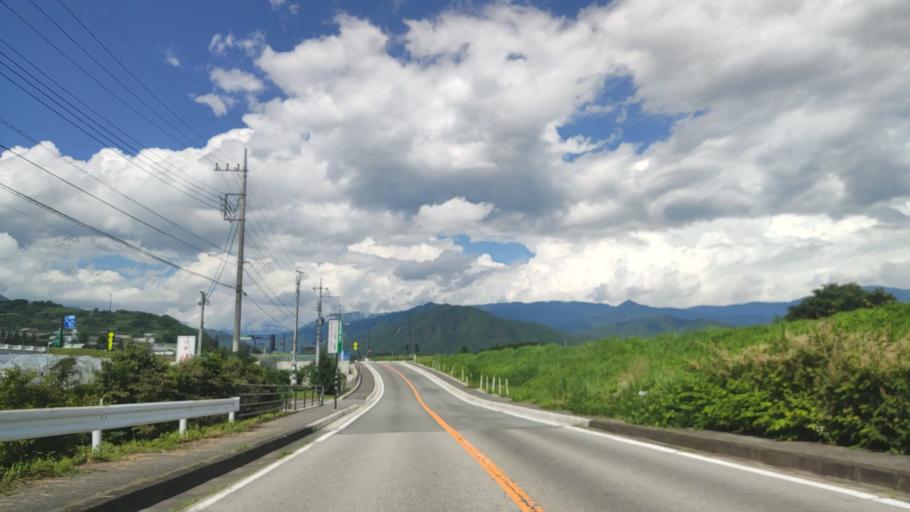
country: JP
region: Yamanashi
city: Enzan
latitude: 35.7085
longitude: 138.6981
